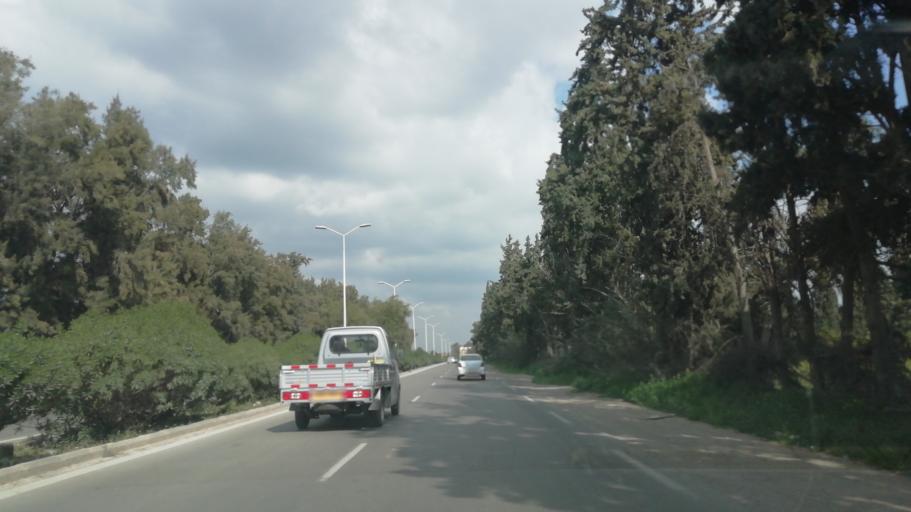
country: DZ
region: Mascara
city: Mascara
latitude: 35.6025
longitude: 0.0863
